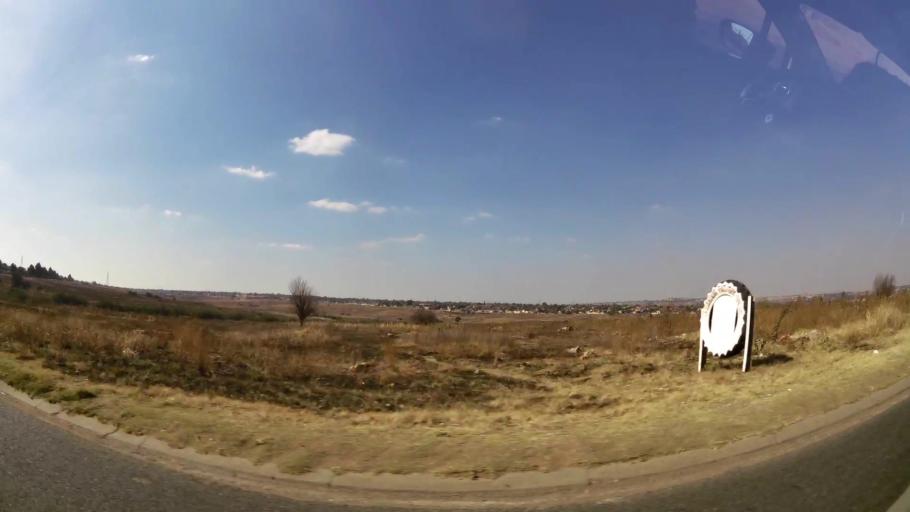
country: ZA
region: Gauteng
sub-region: City of Johannesburg Metropolitan Municipality
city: Roodepoort
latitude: -26.1605
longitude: 27.8051
